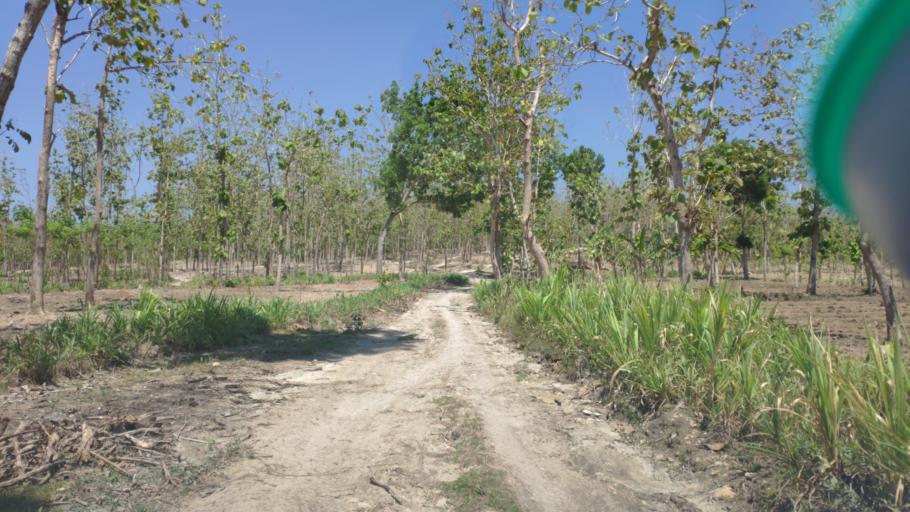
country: ID
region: Central Java
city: Suruhan
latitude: -7.0072
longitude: 111.5256
